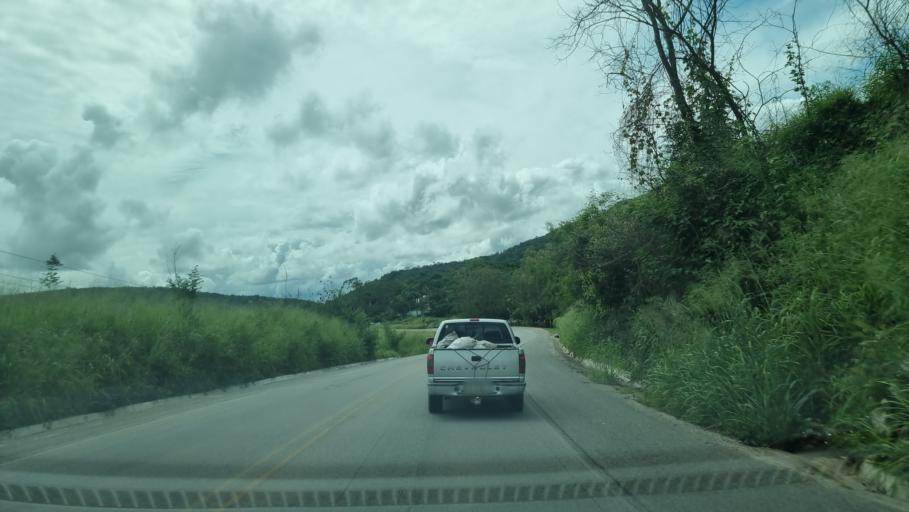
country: BR
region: Pernambuco
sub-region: Caruaru
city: Caruaru
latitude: -8.3737
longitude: -35.9839
